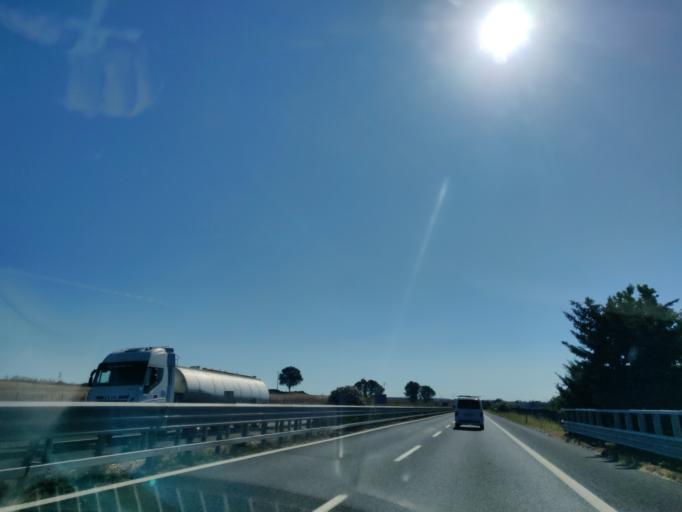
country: IT
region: Latium
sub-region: Citta metropolitana di Roma Capitale
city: Valcanneto
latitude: 41.9355
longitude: 12.1594
